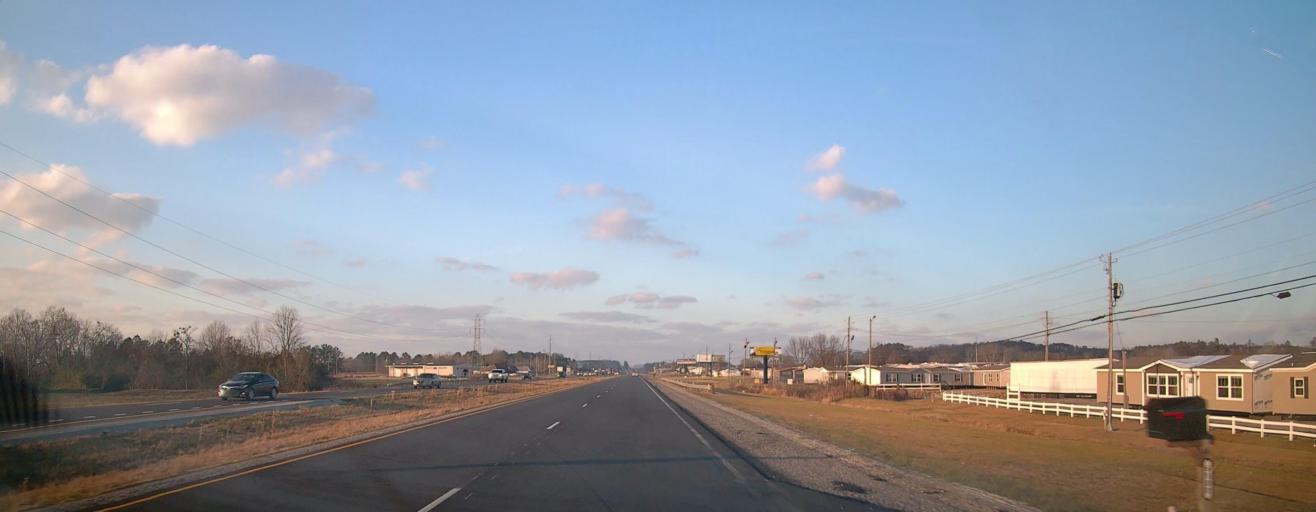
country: US
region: Alabama
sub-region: Calhoun County
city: Alexandria
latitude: 33.7707
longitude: -85.8933
